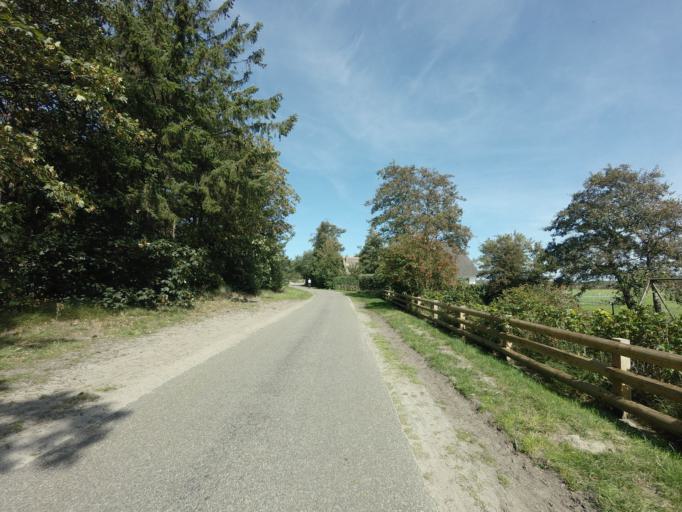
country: NL
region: Friesland
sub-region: Gemeente Ameland
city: Hollum
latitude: 53.4433
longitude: 5.6238
